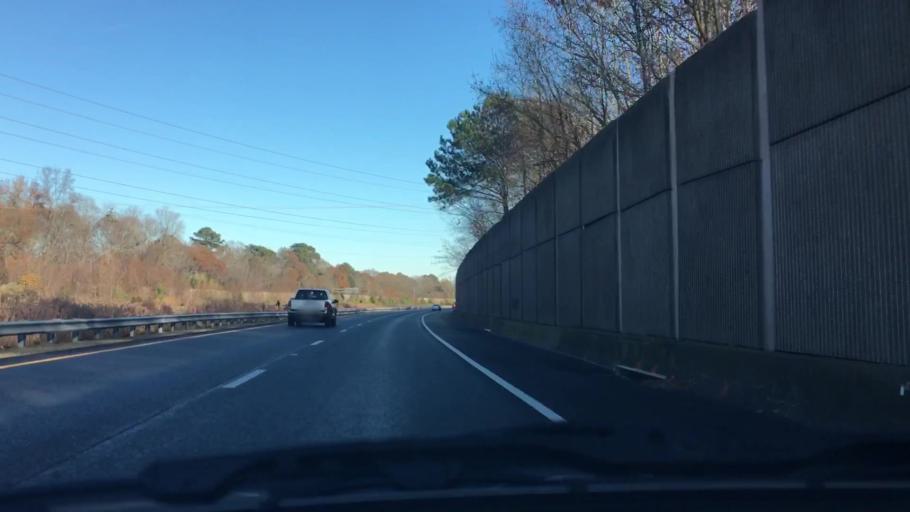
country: US
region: Virginia
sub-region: City of Portsmouth
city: Portsmouth Heights
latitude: 36.8718
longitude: -76.3942
